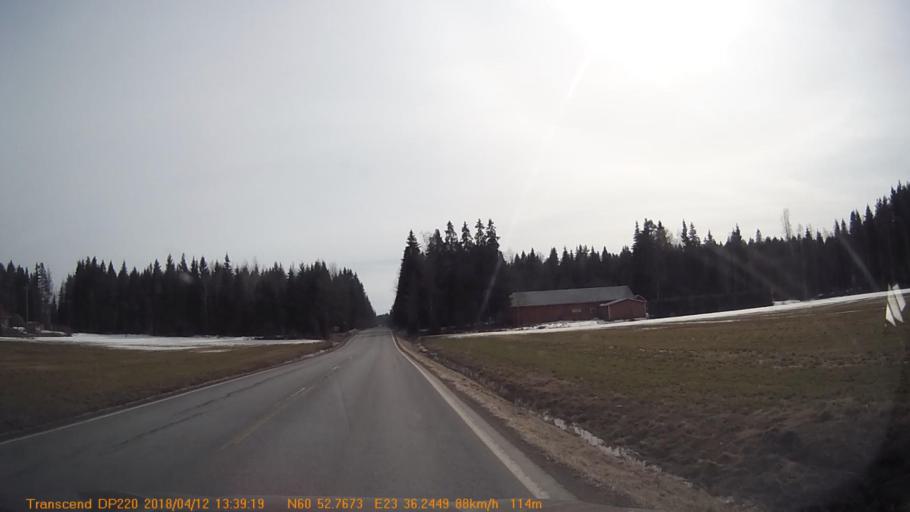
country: FI
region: Haeme
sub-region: Forssa
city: Forssa
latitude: 60.8791
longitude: 23.6042
